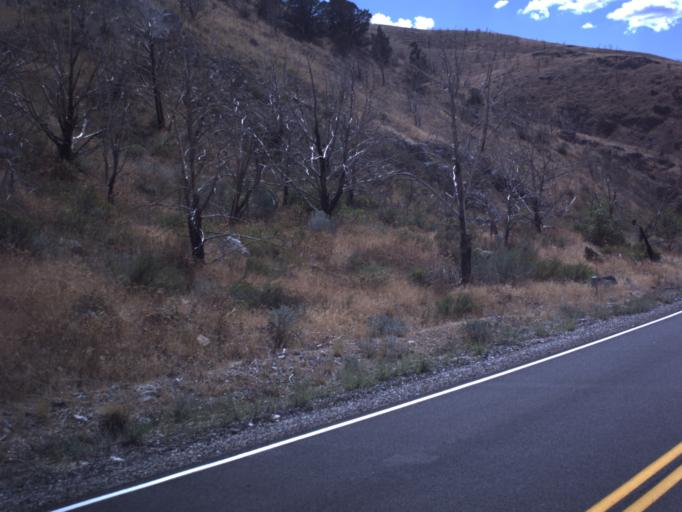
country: US
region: Utah
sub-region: Tooele County
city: Grantsville
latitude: 40.3459
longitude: -112.5930
